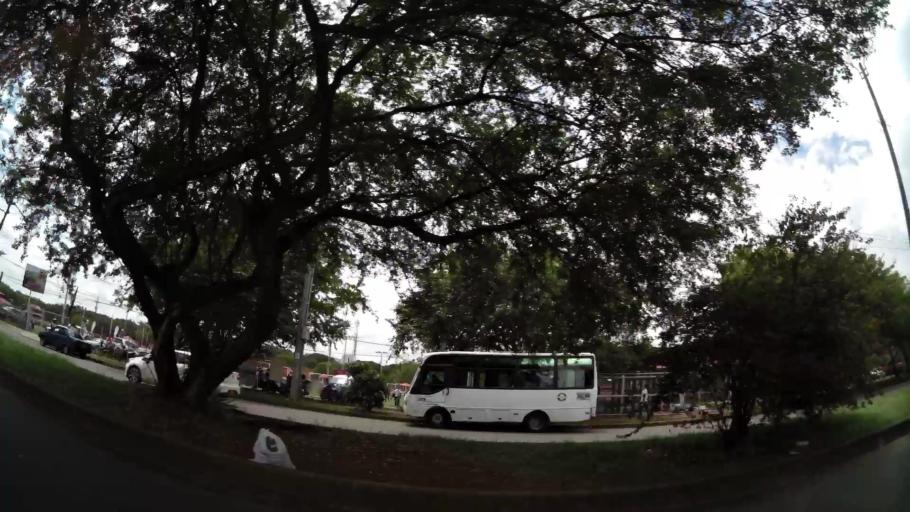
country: CO
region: Valle del Cauca
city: Cali
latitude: 3.3930
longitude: -76.5314
